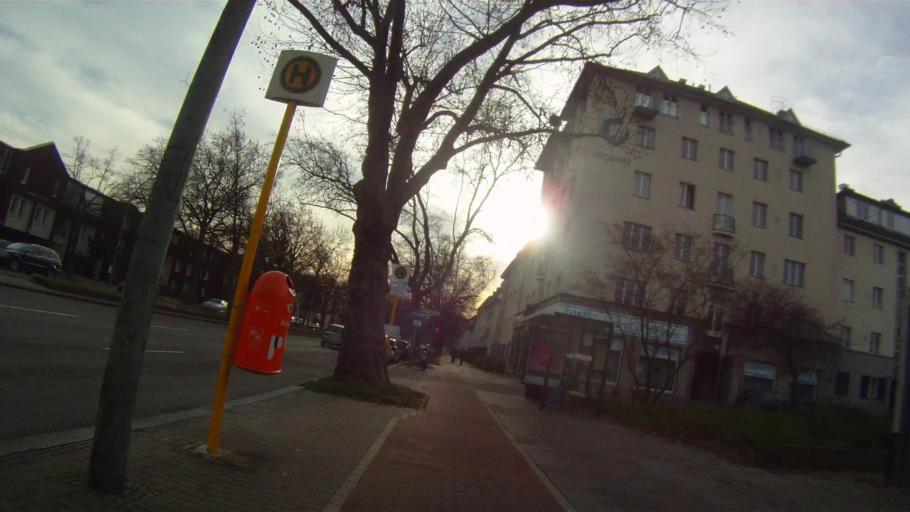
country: DE
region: Berlin
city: Britz
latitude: 52.4522
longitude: 13.4521
